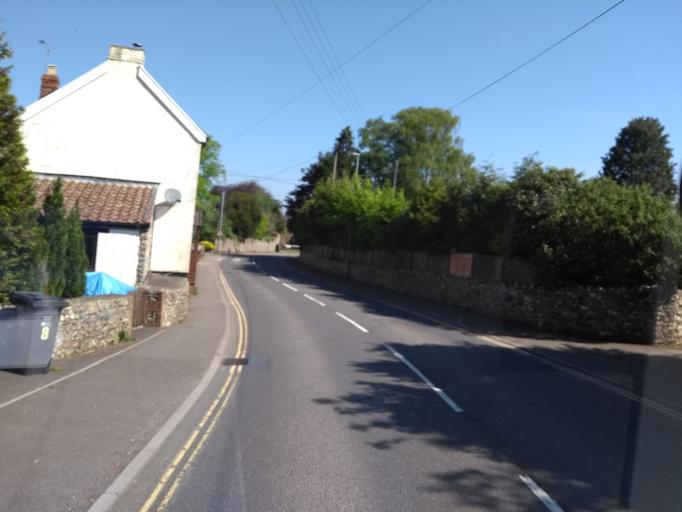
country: GB
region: England
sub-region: Somerset
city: Chard
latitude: 50.8681
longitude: -2.9636
